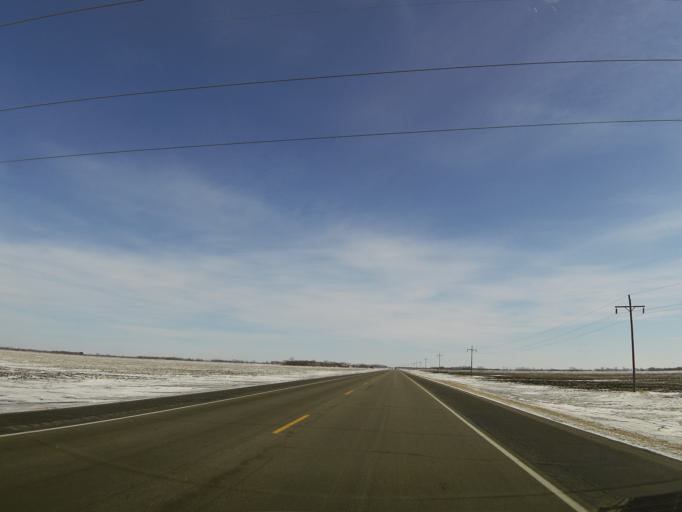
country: US
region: North Dakota
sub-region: Walsh County
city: Grafton
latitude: 48.4121
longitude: -97.2669
